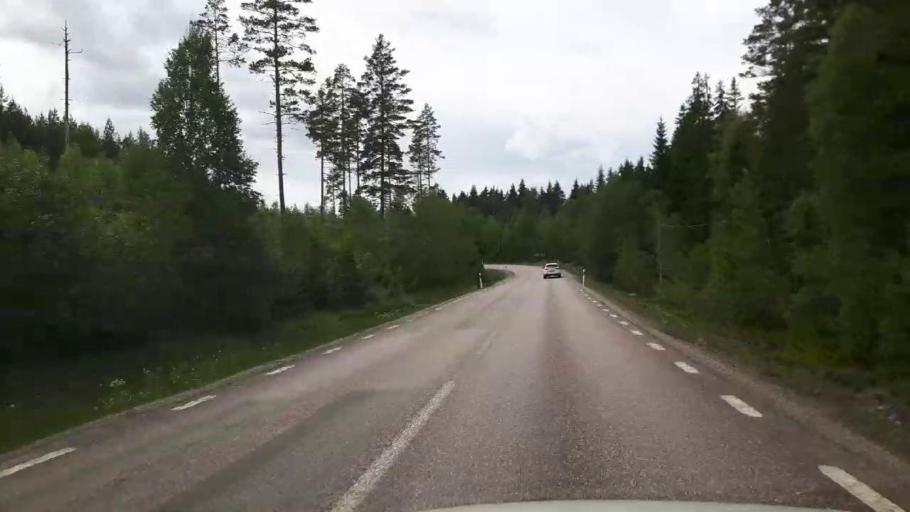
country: SE
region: Vaestmanland
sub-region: Norbergs Kommun
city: Norberg
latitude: 60.1274
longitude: 15.9218
